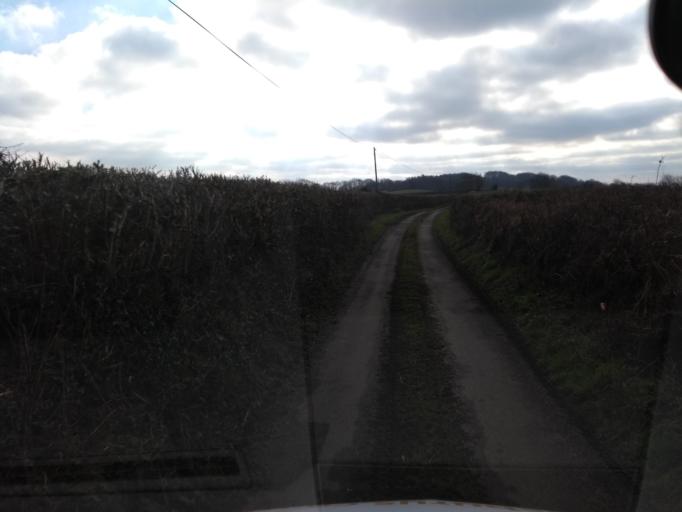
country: GB
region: England
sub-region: Somerset
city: Creech Saint Michael
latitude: 50.9339
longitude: -3.0341
